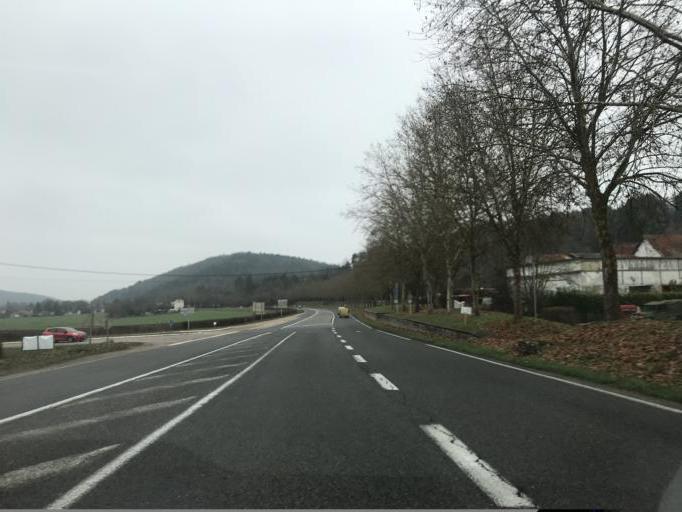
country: FR
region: Bourgogne
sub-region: Departement de l'Yonne
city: Avallon
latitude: 47.5263
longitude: 3.7951
